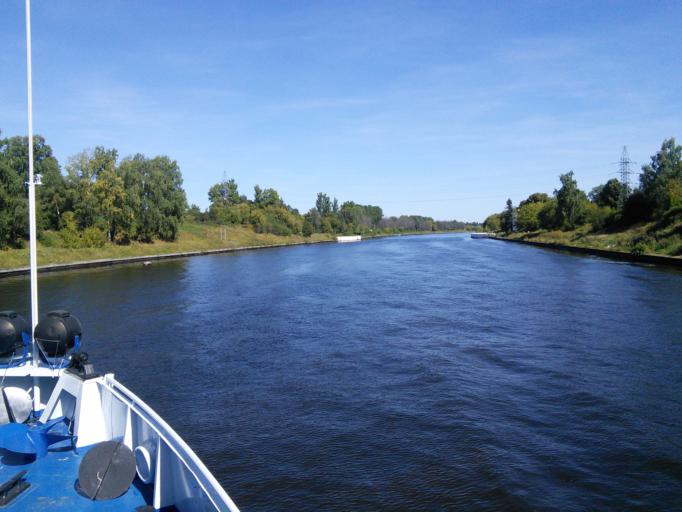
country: RU
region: Moskovskaya
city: Dolgoprudnyy
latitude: 55.9471
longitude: 37.4794
